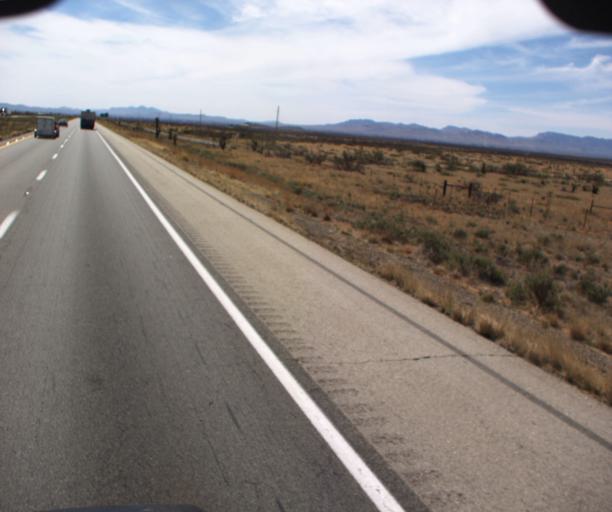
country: US
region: Arizona
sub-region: Cochise County
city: Willcox
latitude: 32.3266
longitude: -109.7733
